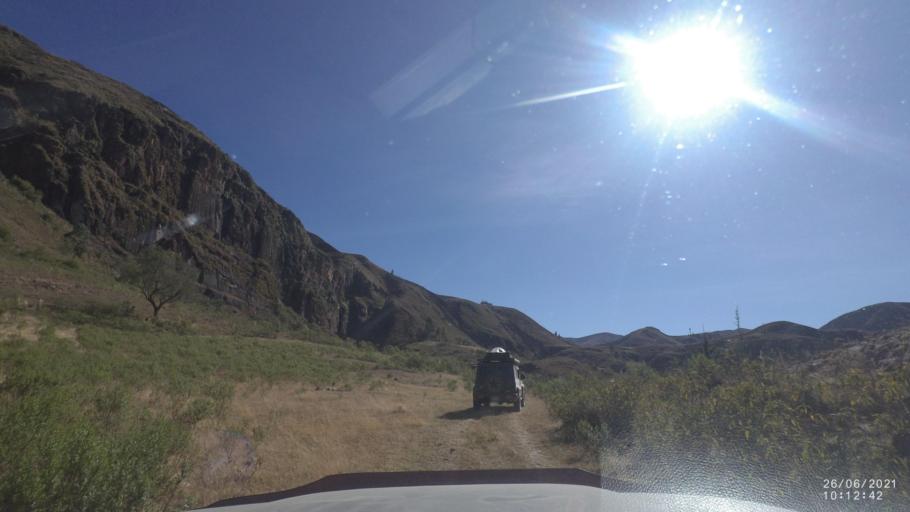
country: BO
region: Cochabamba
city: Mizque
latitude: -17.9140
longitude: -65.6255
